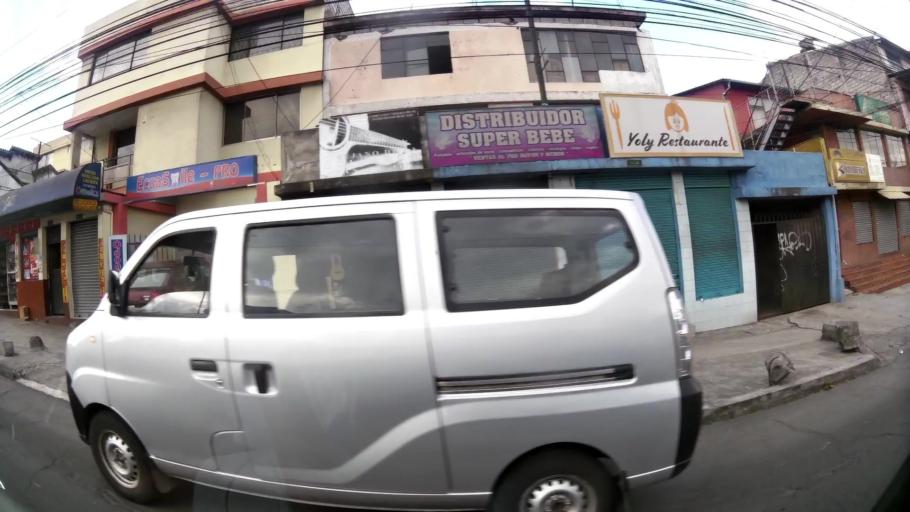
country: EC
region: Pichincha
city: Quito
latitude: -0.1408
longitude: -78.4827
